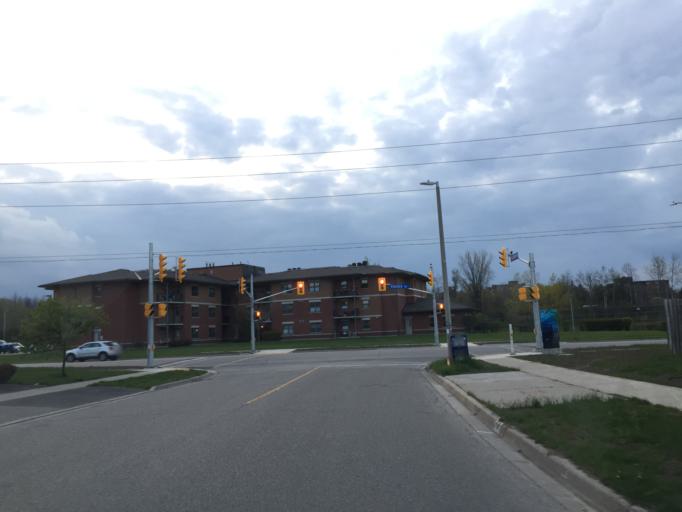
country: CA
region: Ontario
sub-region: Wellington County
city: Guelph
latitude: 43.5293
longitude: -80.2779
